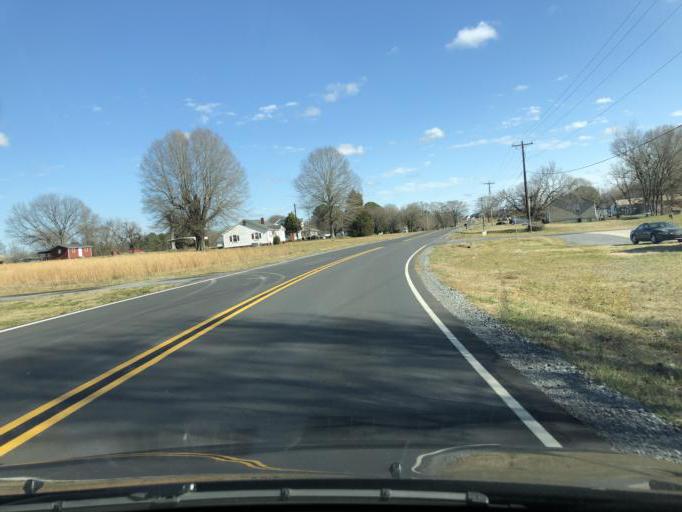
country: US
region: North Carolina
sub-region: Cleveland County
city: Shelby
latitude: 35.2060
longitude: -81.5559
